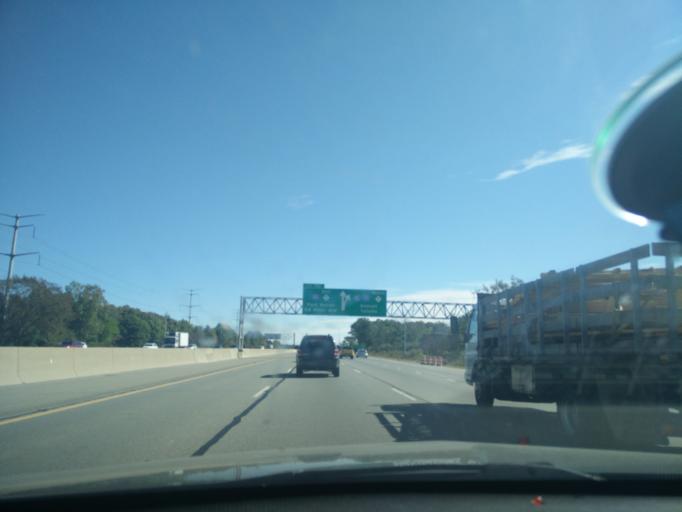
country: US
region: Michigan
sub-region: Oakland County
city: Novi
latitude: 42.4860
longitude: -83.4655
